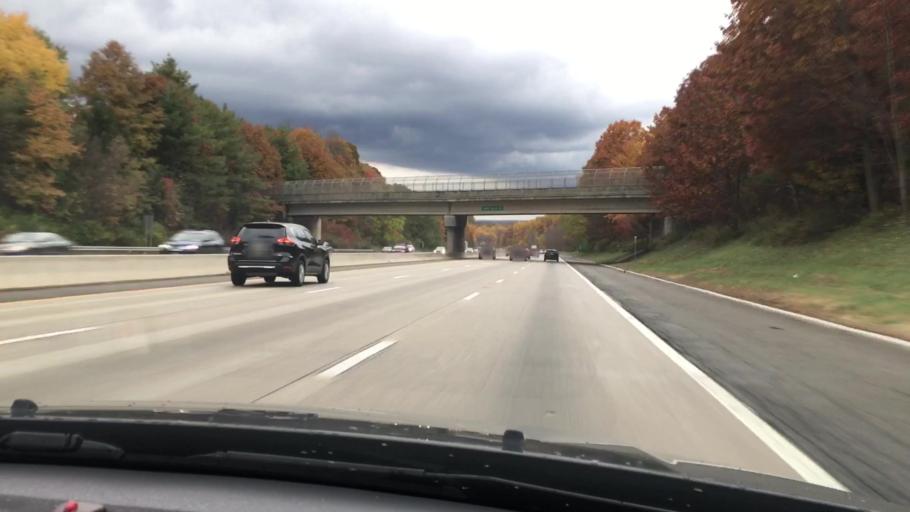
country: US
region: New Jersey
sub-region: Morris County
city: Lincoln Park
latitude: 40.9505
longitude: -74.3430
